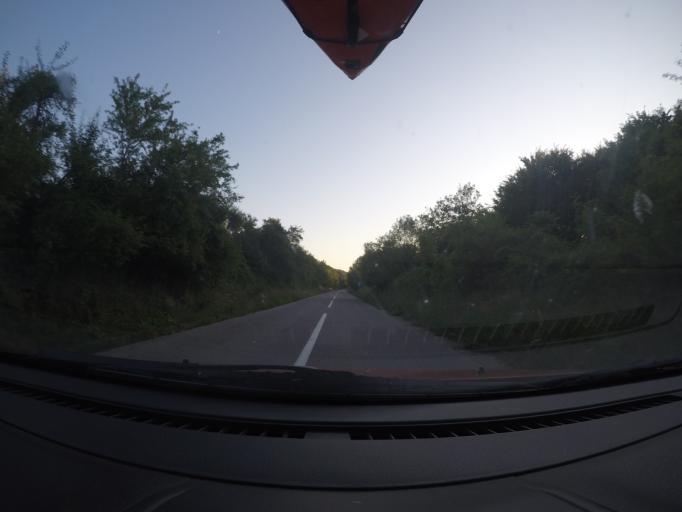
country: RO
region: Mehedinti
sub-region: Comuna Eselnita
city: Eselnita
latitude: 44.6705
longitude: 22.3776
